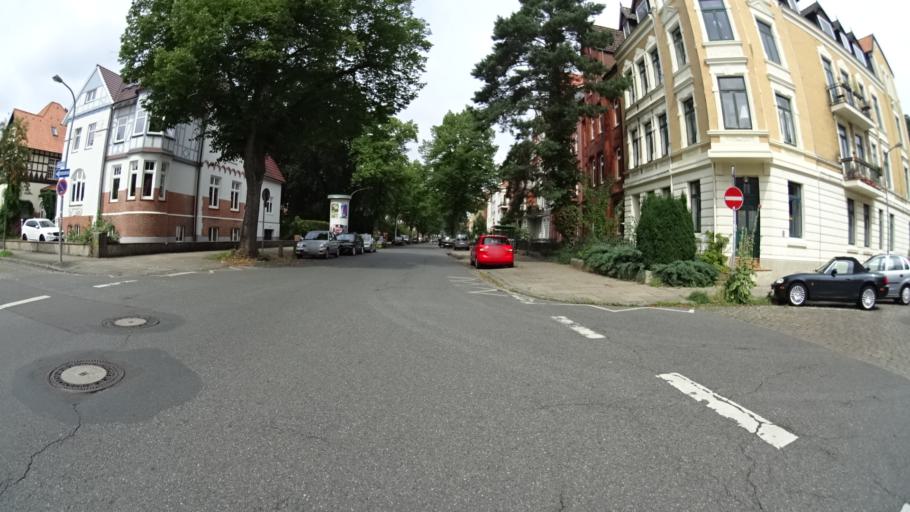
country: DE
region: Lower Saxony
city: Lueneburg
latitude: 53.2409
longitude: 10.4103
